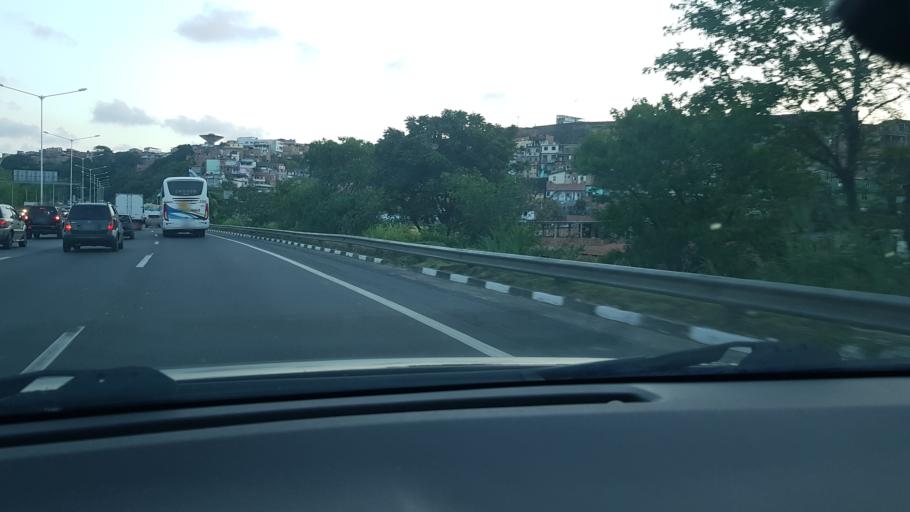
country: BR
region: Bahia
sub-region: Salvador
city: Salvador
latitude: -12.9314
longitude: -38.4710
